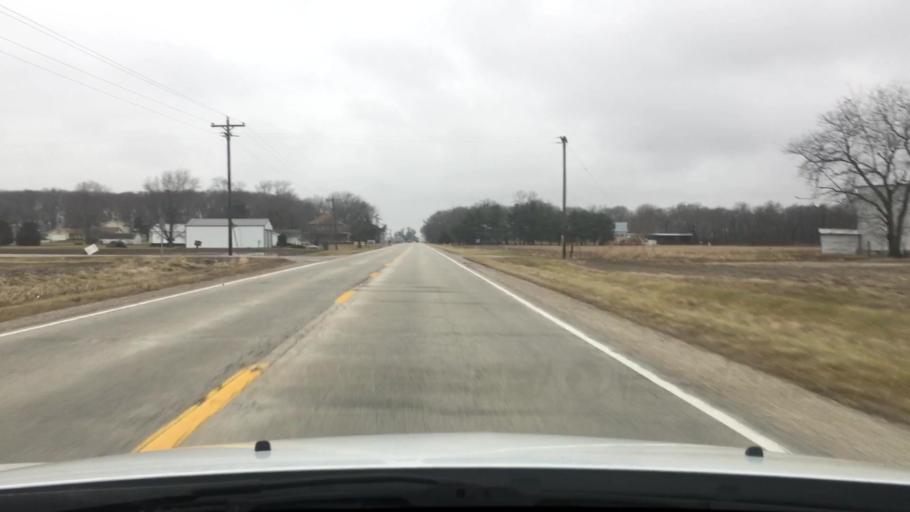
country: US
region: Illinois
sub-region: Iroquois County
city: Clifton
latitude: 40.8879
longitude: -87.8268
